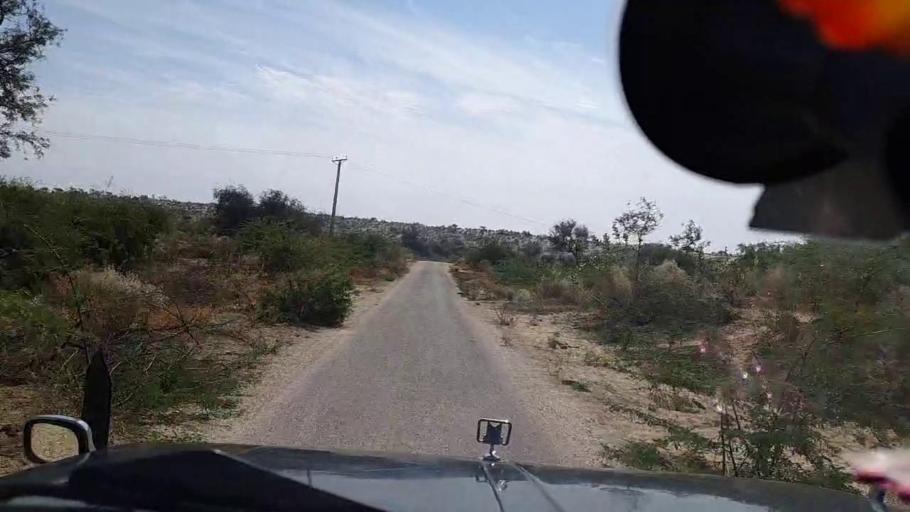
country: PK
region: Sindh
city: Diplo
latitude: 24.4053
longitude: 69.5863
